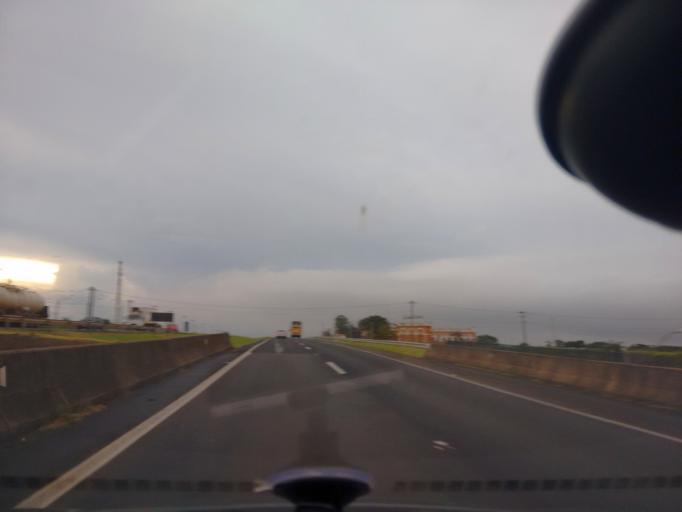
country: BR
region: Sao Paulo
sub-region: Sao Carlos
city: Sao Carlos
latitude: -21.9762
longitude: -47.9327
